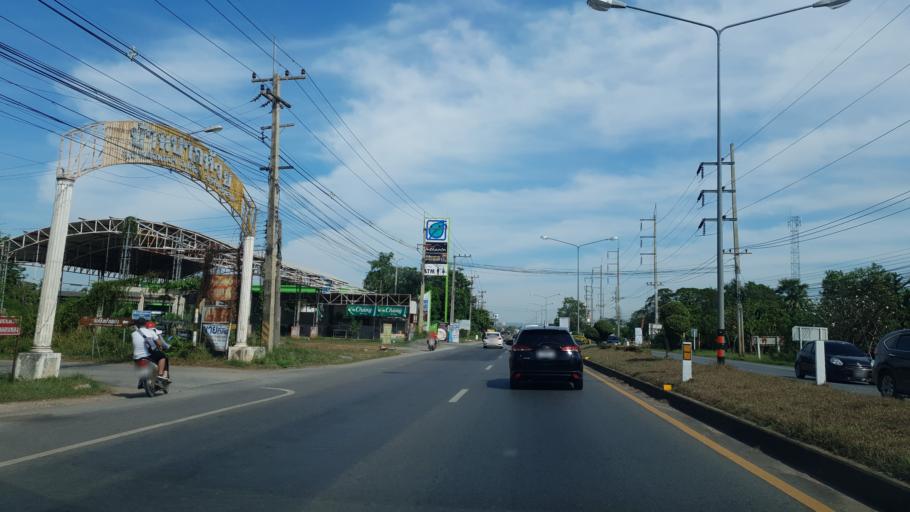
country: TH
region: Phitsanulok
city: Wang Thong
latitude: 16.8506
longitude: 100.3470
